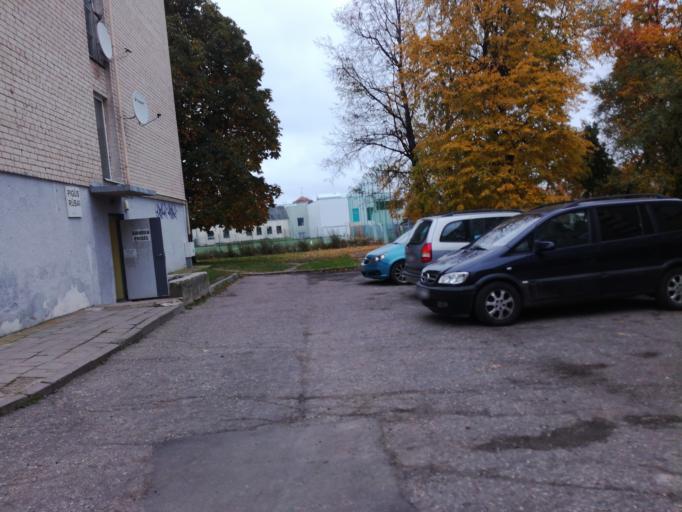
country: LT
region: Alytaus apskritis
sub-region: Alytus
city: Alytus
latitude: 54.3968
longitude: 24.0333
